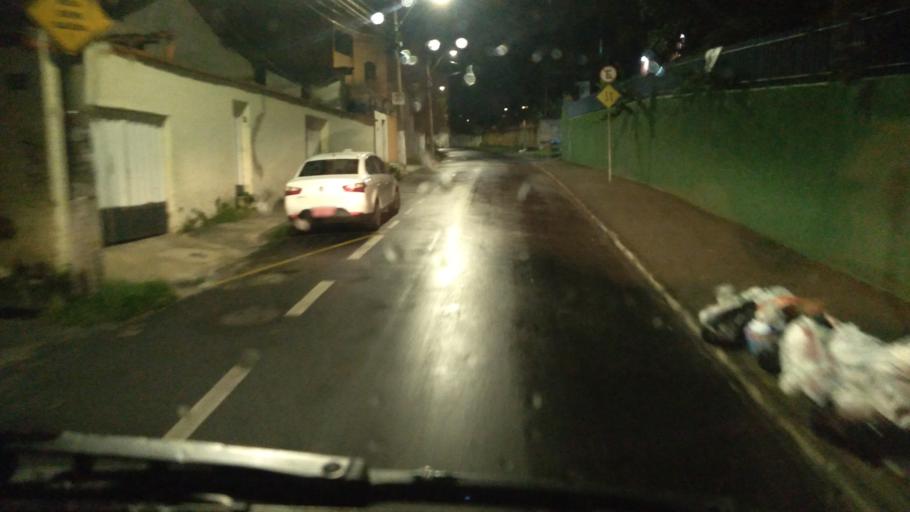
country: BR
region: Minas Gerais
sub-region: Belo Horizonte
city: Belo Horizonte
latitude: -19.8982
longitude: -43.9138
